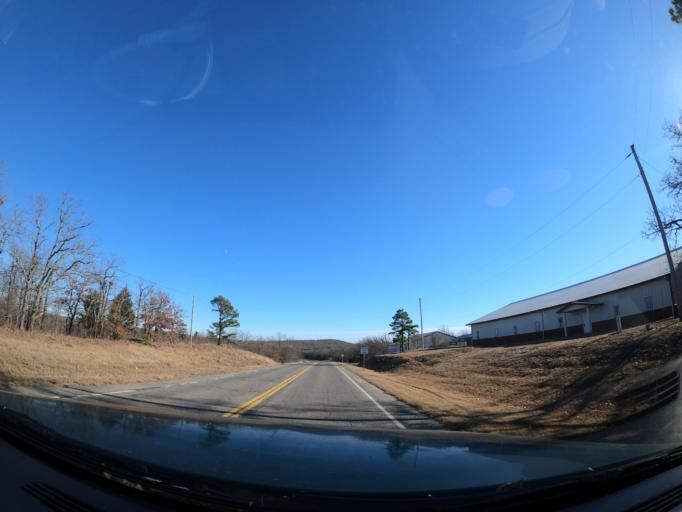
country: US
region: Oklahoma
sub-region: Pittsburg County
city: Longtown
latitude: 35.2284
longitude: -95.4510
